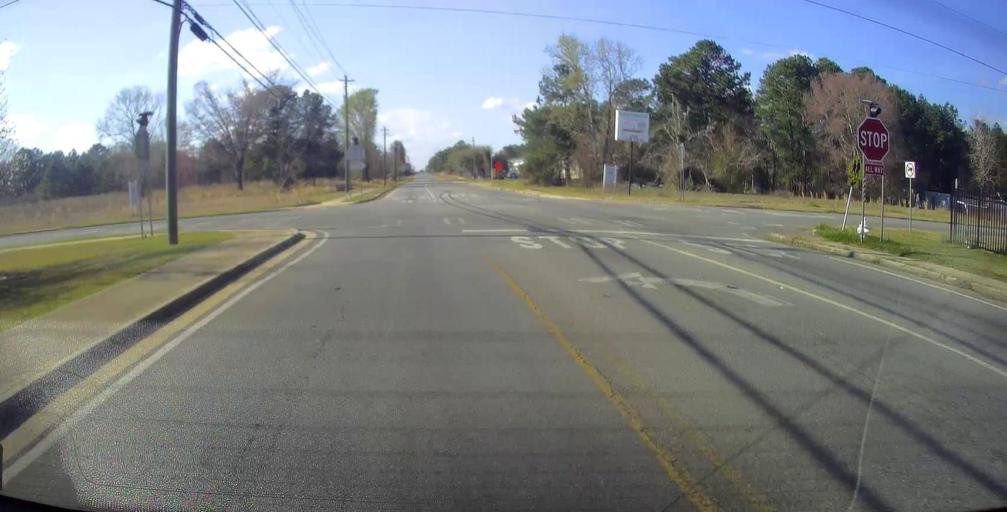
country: US
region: Georgia
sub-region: Laurens County
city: Dublin
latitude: 32.5446
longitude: -82.9207
